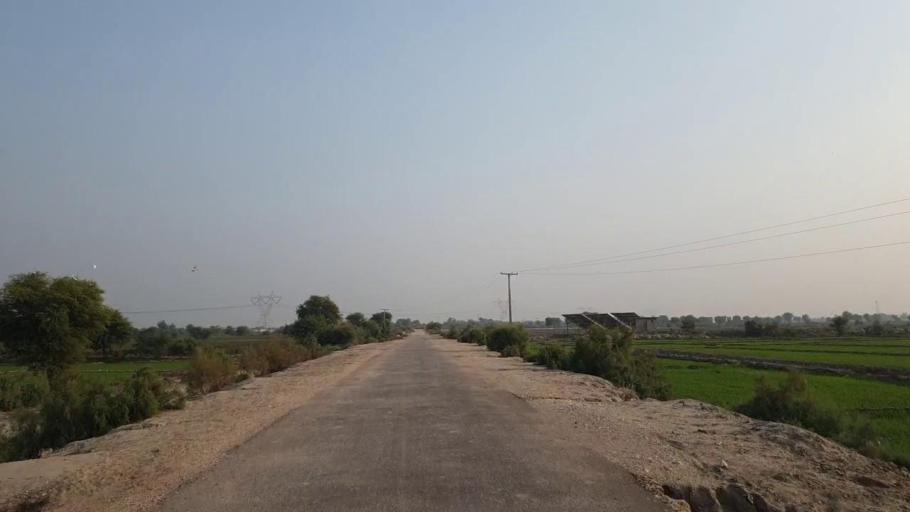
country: PK
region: Sindh
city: Bhan
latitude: 26.4964
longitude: 67.7682
